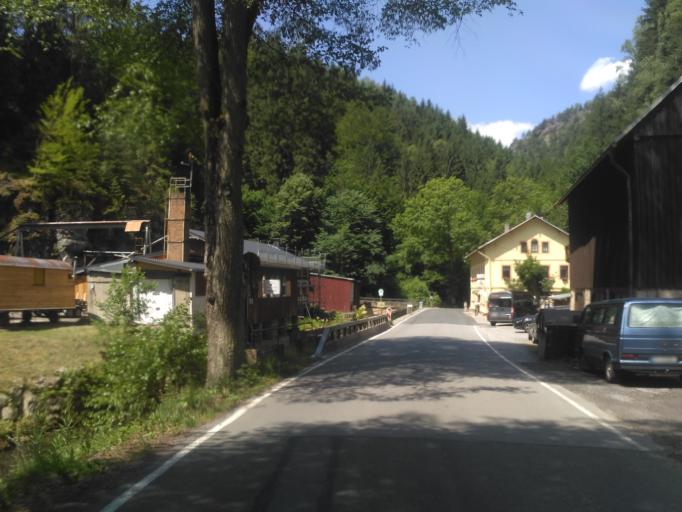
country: DE
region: Saxony
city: Sebnitz
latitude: 50.9254
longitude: 14.2767
